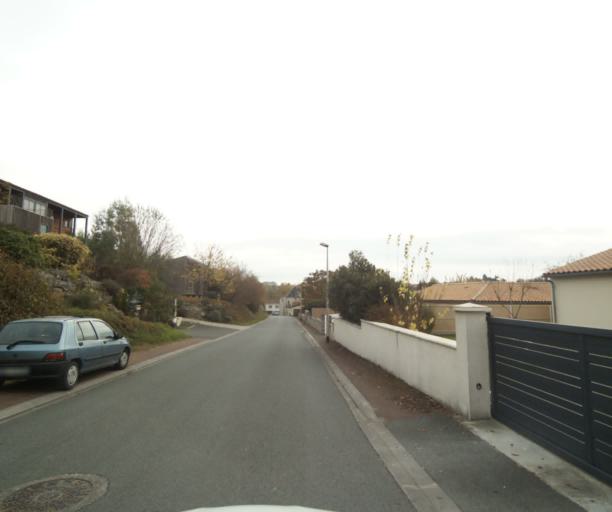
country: FR
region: Poitou-Charentes
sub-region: Departement de la Charente-Maritime
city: Saintes
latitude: 45.7426
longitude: -0.6523
